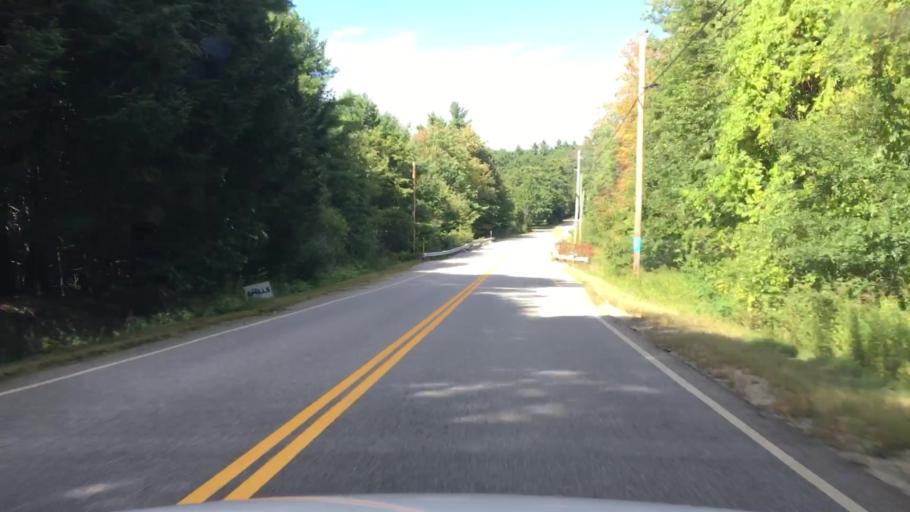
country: US
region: Maine
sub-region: Cumberland County
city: West Scarborough
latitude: 43.6267
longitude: -70.4086
